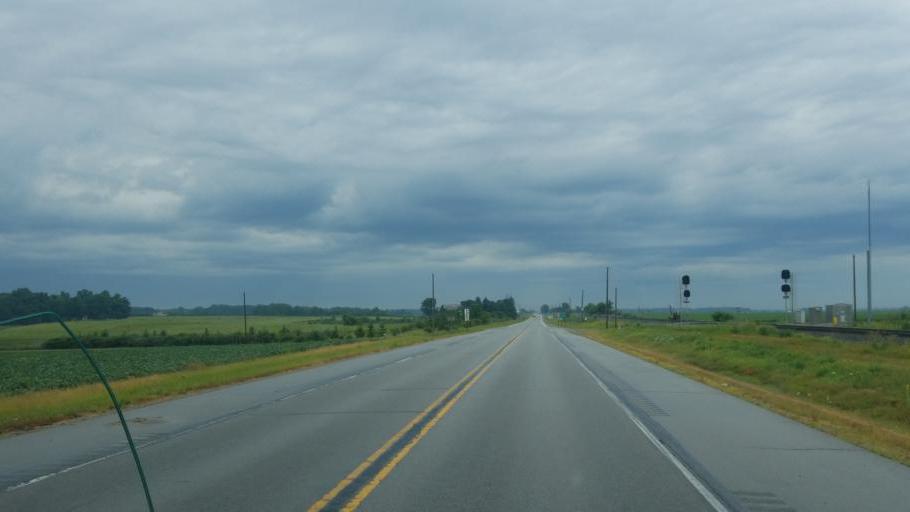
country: US
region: Ohio
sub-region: Williams County
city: Edgerton
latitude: 41.4385
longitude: -84.8055
